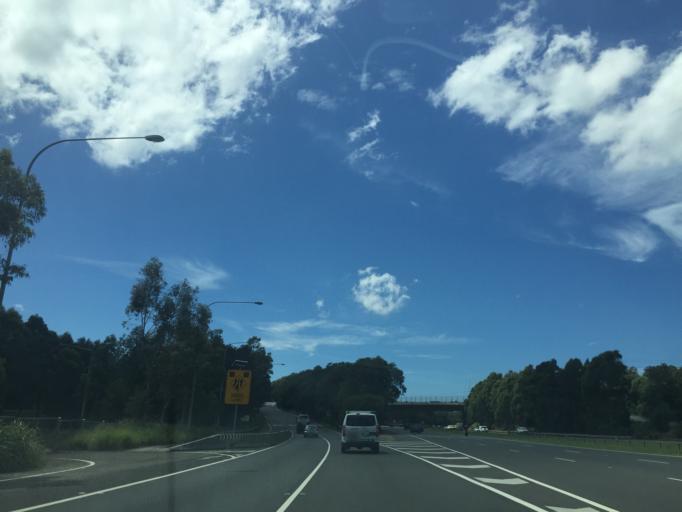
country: AU
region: New South Wales
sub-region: Strathfield
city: Homebush
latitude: -33.8562
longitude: 151.0670
